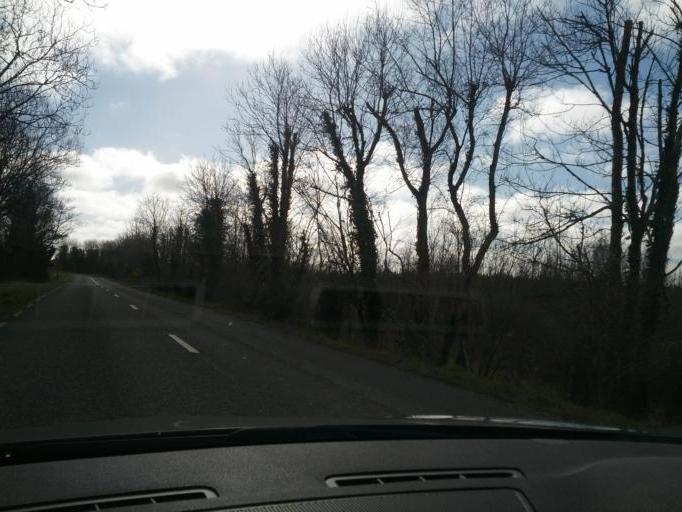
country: IE
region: Connaught
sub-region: County Galway
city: Ballinasloe
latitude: 53.4196
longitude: -8.3878
